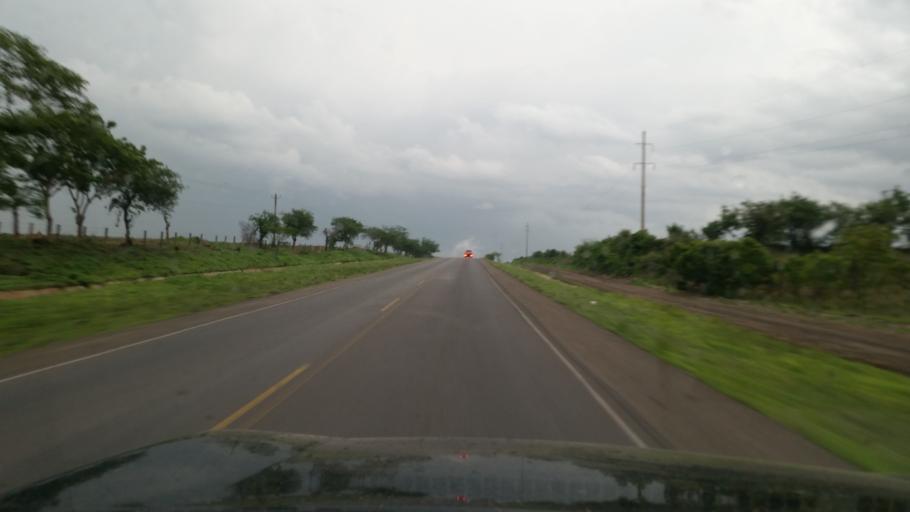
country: NI
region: Chinandega
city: Puerto Morazan
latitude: 12.7904
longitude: -87.0195
